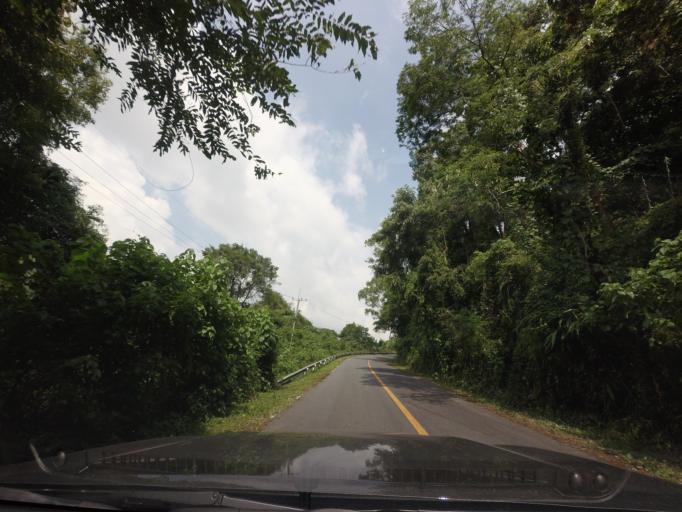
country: TH
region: Nan
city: Pua
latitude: 19.1854
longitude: 101.0018
